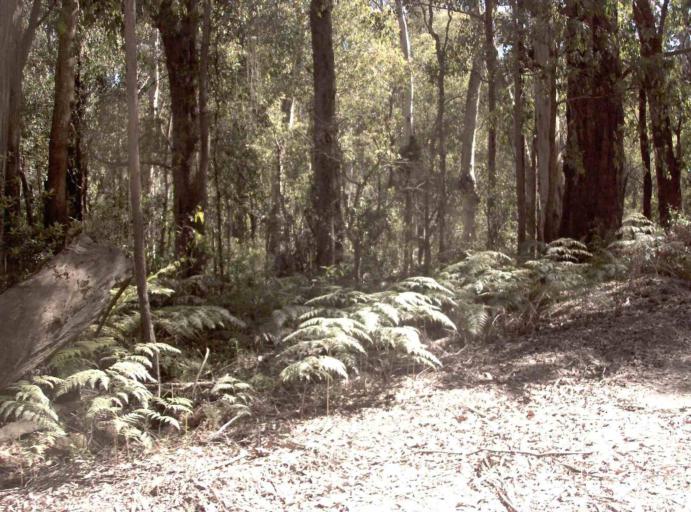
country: AU
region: New South Wales
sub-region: Bombala
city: Bombala
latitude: -37.2476
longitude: 148.7482
